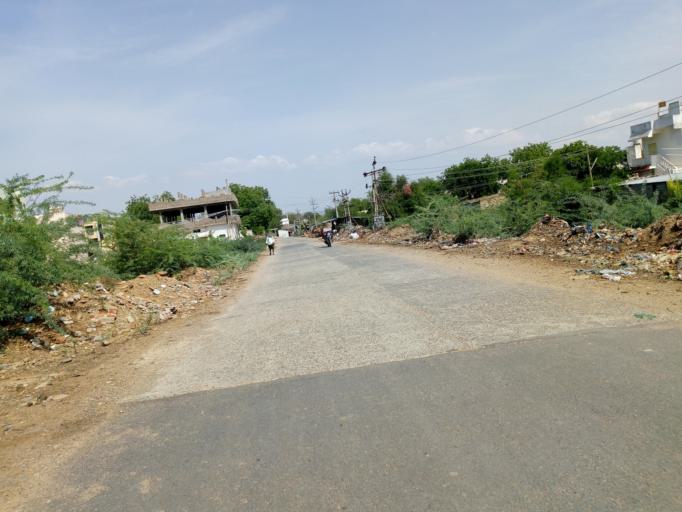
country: IN
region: Andhra Pradesh
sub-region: Prakasam
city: Cumbum
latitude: 15.5844
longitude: 79.1097
